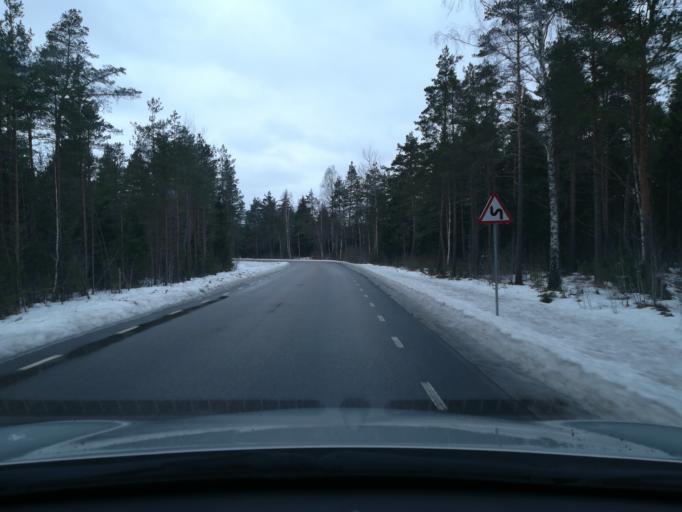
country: EE
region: Harju
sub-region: Nissi vald
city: Riisipere
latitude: 59.1437
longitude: 24.2943
